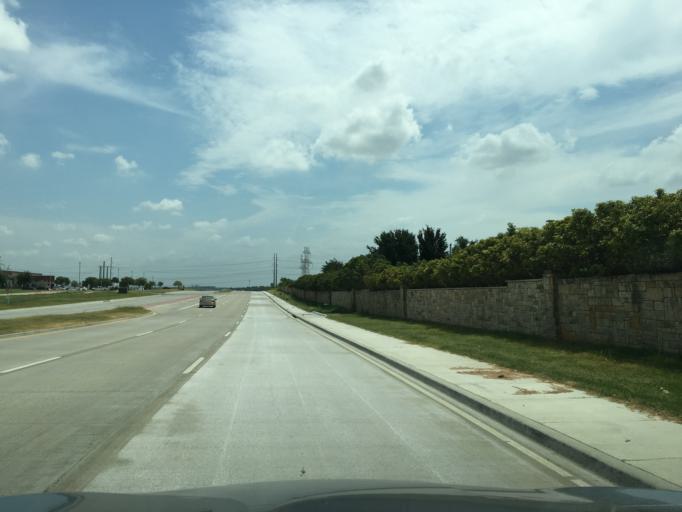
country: US
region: Texas
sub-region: Denton County
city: The Colony
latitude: 33.0462
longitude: -96.9105
